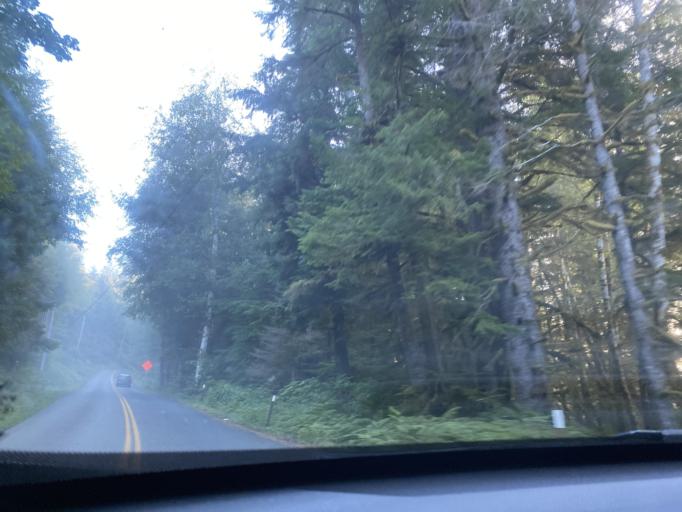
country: US
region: Washington
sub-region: Clallam County
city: Forks
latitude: 47.8111
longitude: -124.0771
